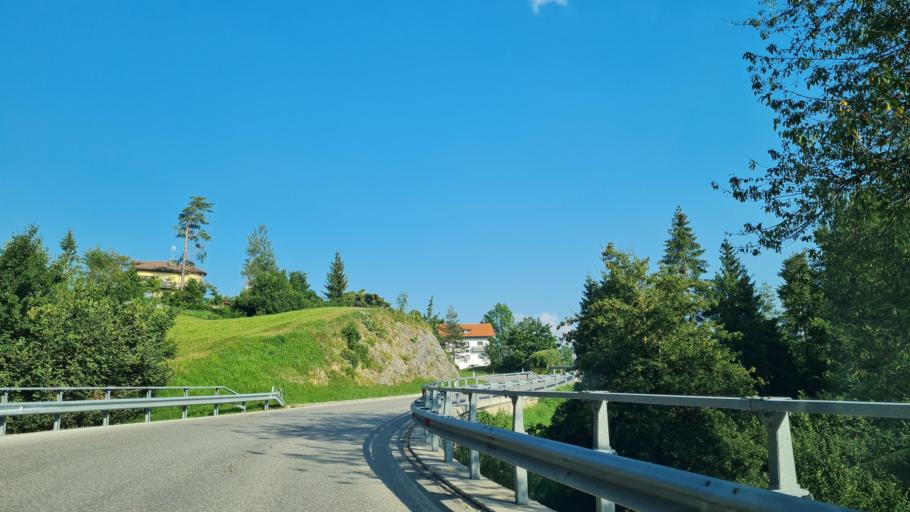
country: IT
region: Trentino-Alto Adige
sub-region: Provincia di Trento
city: Gionghi-Cappella
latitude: 45.9409
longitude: 11.2651
